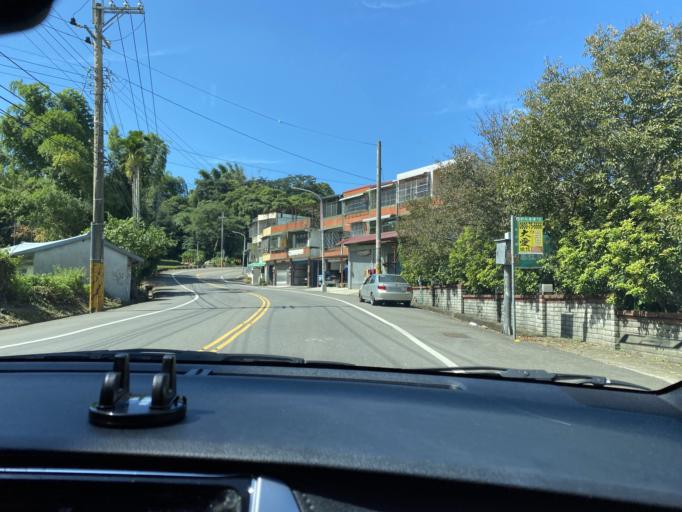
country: TW
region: Taiwan
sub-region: Nantou
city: Nantou
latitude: 23.8553
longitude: 120.6290
